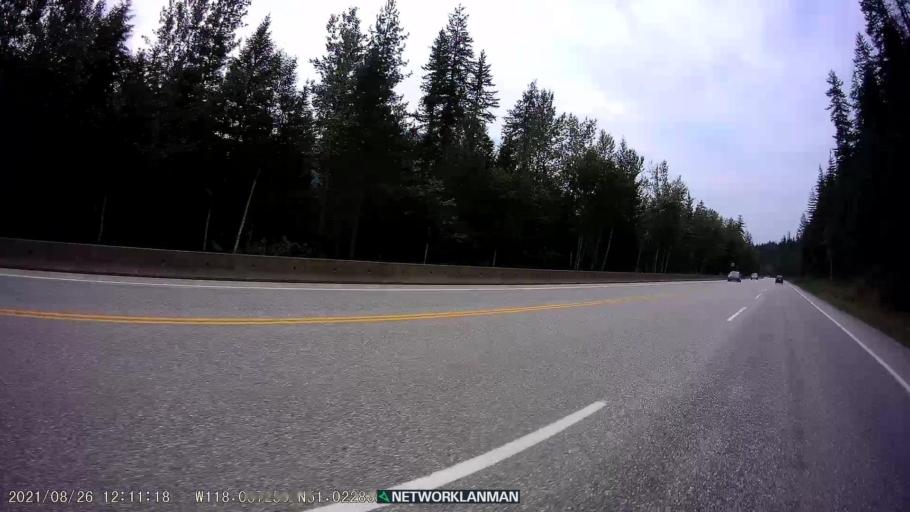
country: CA
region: British Columbia
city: Revelstoke
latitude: 51.0228
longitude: -118.0576
